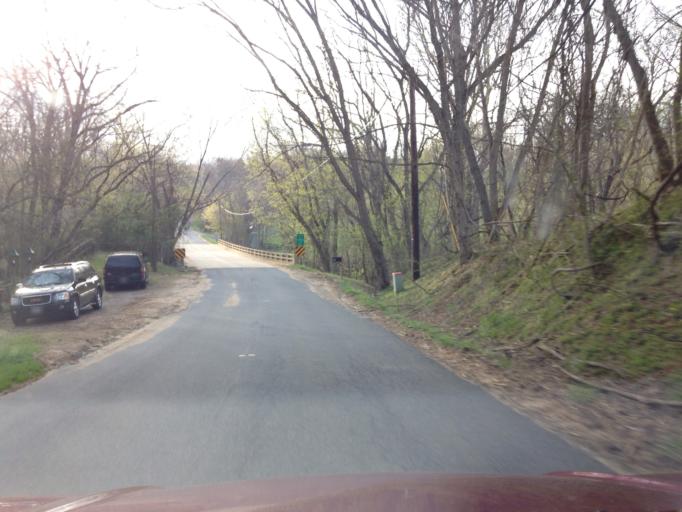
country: US
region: Maryland
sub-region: Frederick County
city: Point of Rocks
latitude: 39.2544
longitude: -77.5748
